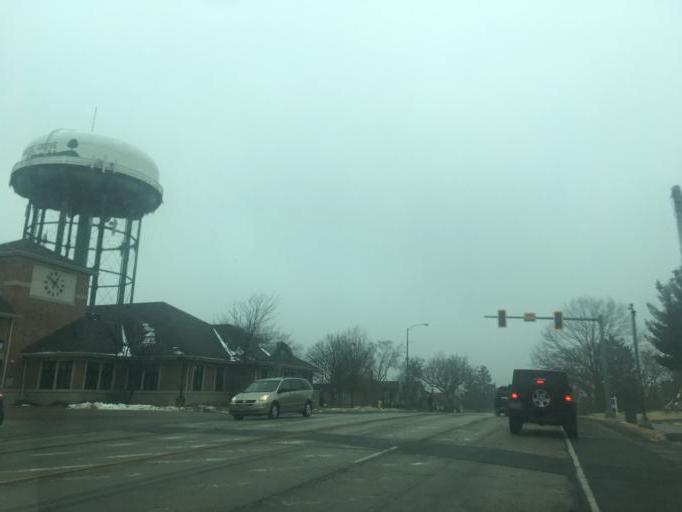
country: US
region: Illinois
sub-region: DuPage County
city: Downers Grove
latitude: 41.7880
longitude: -88.0091
